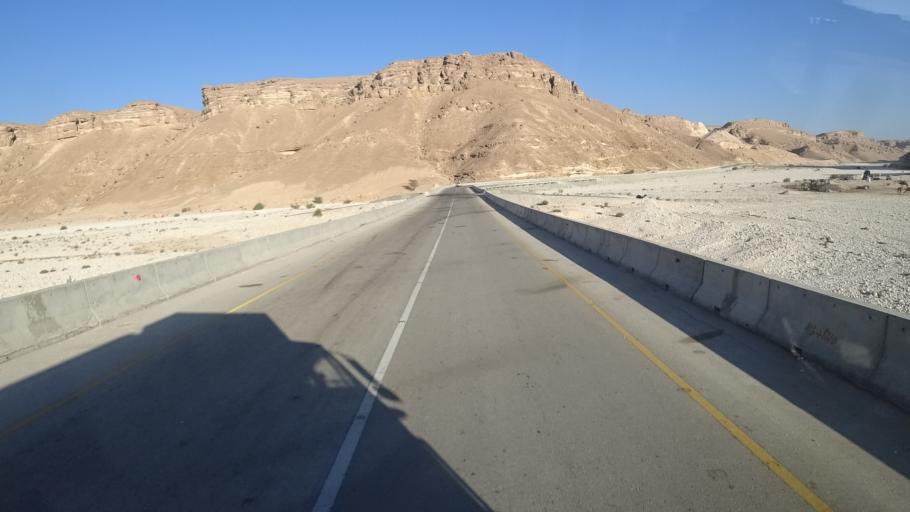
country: YE
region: Al Mahrah
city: Hawf
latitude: 17.0984
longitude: 53.0490
